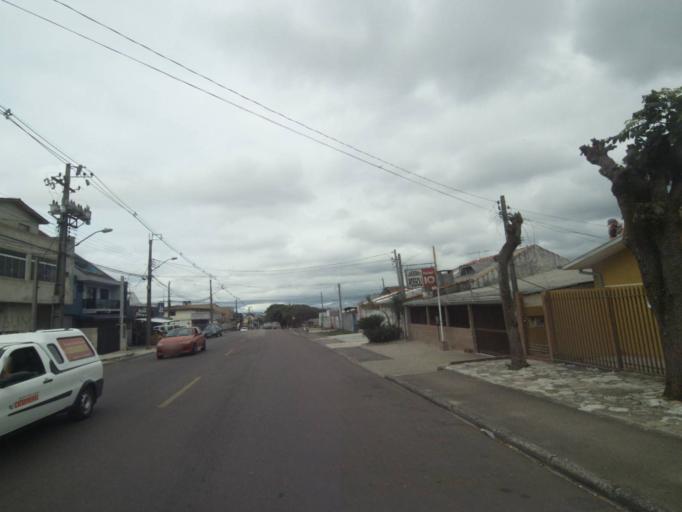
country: BR
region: Parana
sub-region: Sao Jose Dos Pinhais
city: Sao Jose dos Pinhais
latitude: -25.5447
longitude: -49.2856
